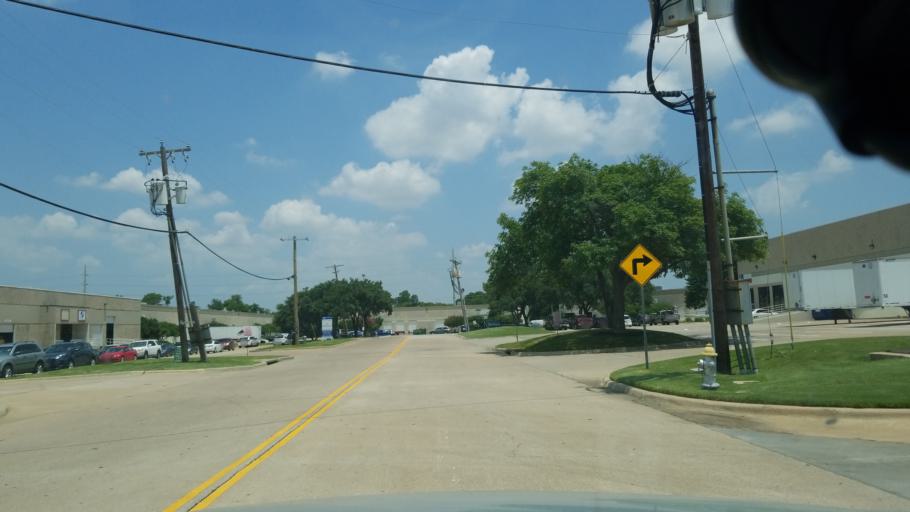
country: US
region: Texas
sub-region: Dallas County
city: Carrollton
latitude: 32.9564
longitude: -96.8609
